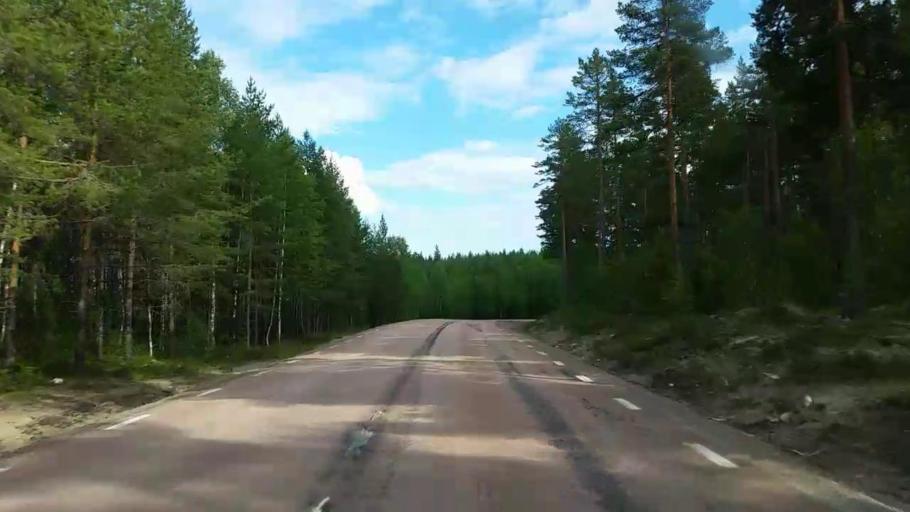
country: SE
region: Gaevleborg
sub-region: Ljusdals Kommun
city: Farila
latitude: 61.9656
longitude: 15.8763
